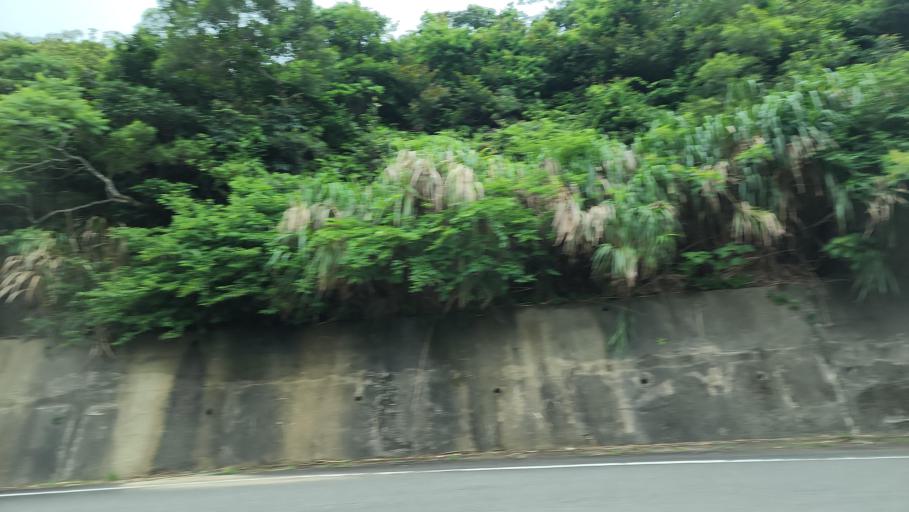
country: TW
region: Taiwan
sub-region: Keelung
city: Keelung
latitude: 25.1989
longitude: 121.6811
